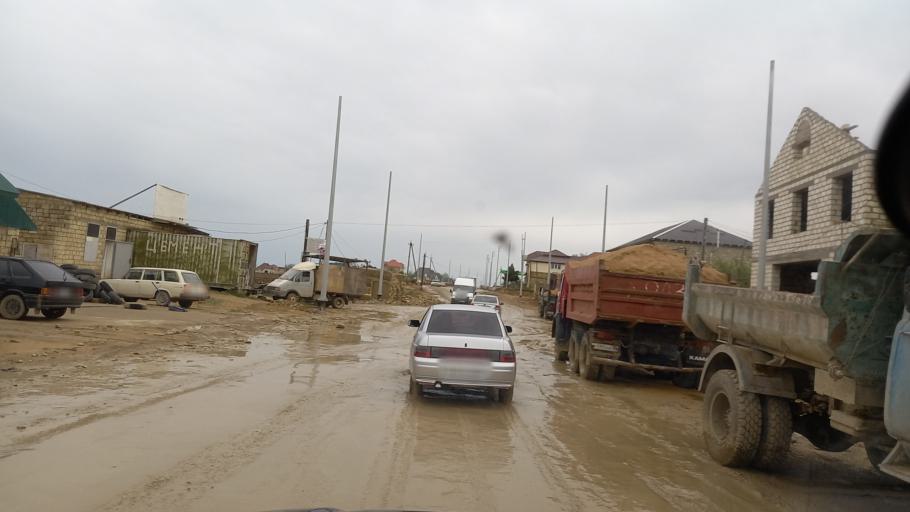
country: RU
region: Dagestan
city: Derbent
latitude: 42.1012
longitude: 48.2840
